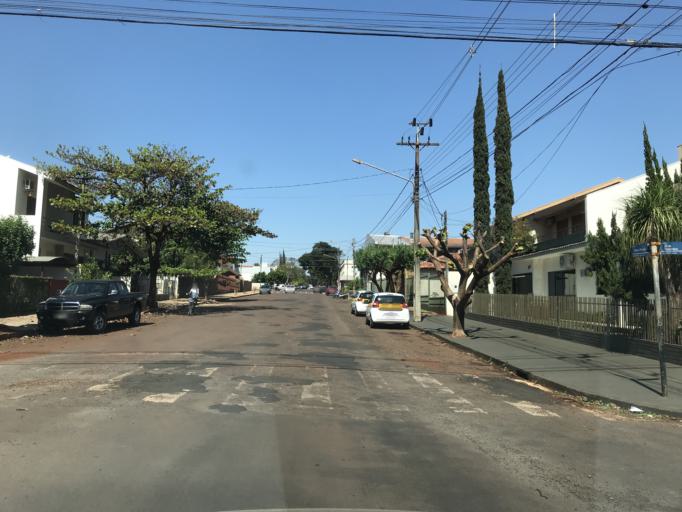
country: BR
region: Parana
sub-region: Palotina
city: Palotina
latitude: -24.2829
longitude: -53.8438
